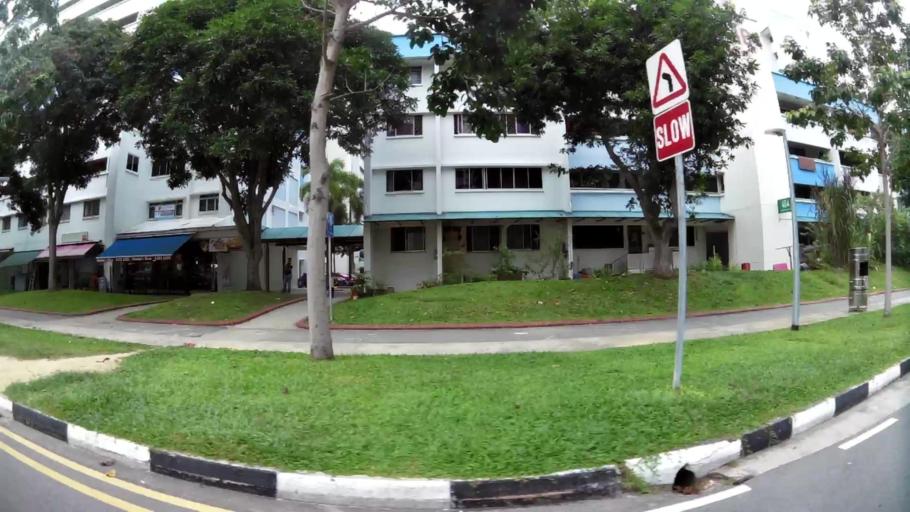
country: SG
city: Singapore
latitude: 1.3596
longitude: 103.9554
